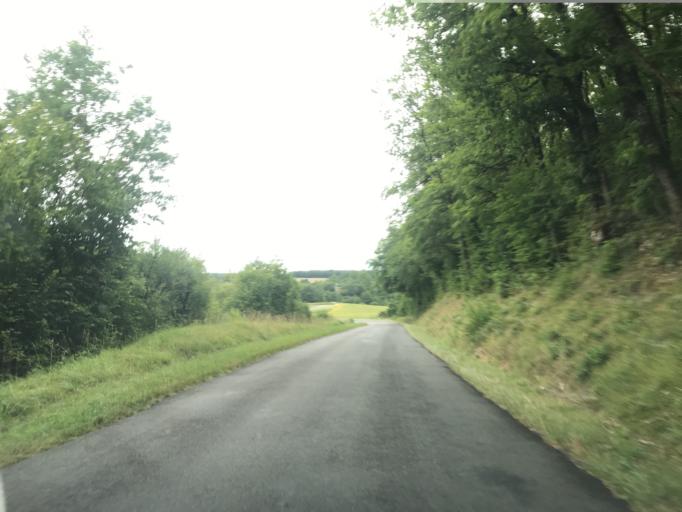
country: FR
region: Poitou-Charentes
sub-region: Departement de la Charente
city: Dirac
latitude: 45.5692
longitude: 0.2117
